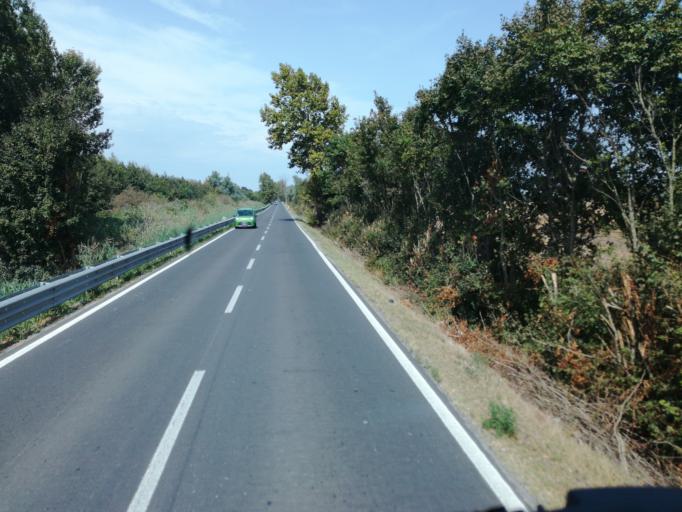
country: IT
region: Veneto
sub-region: Provincia di Venezia
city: Pegolotte
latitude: 45.1632
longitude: 12.0488
